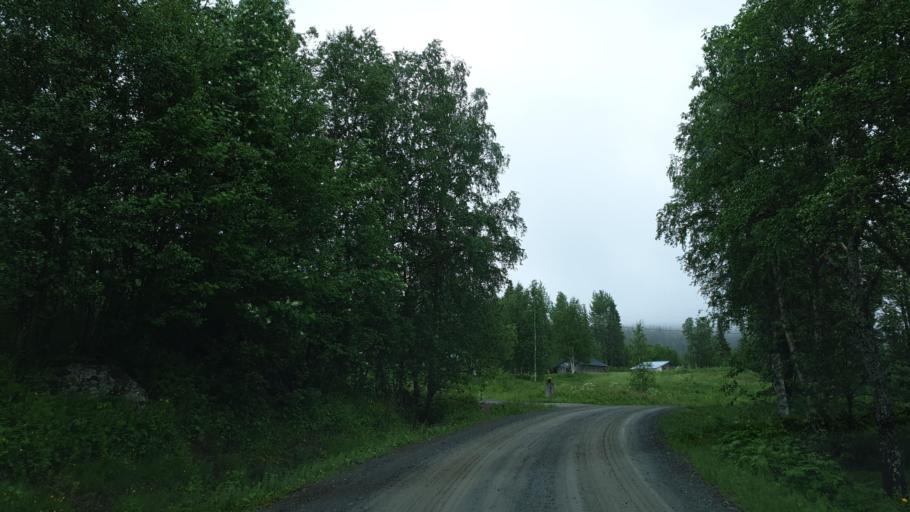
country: SE
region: Vaesterbotten
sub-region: Vilhelmina Kommun
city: Sjoberg
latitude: 65.3454
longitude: 15.8666
